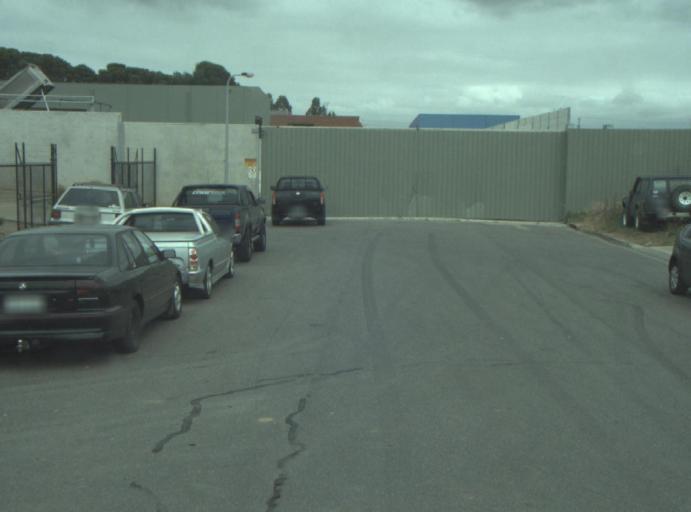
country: AU
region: Victoria
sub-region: Greater Geelong
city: Breakwater
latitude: -38.1932
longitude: 144.3459
